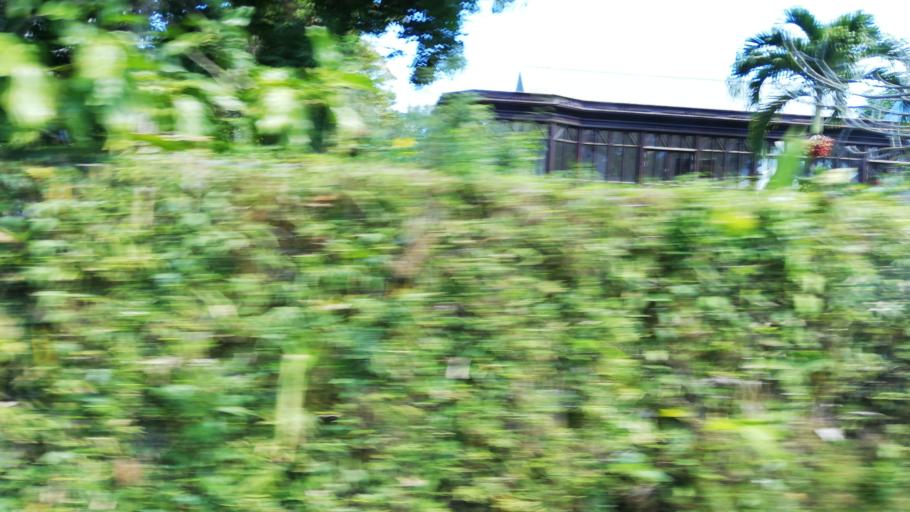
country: MU
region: Plaines Wilhems
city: Ebene
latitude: -20.2303
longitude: 57.4715
